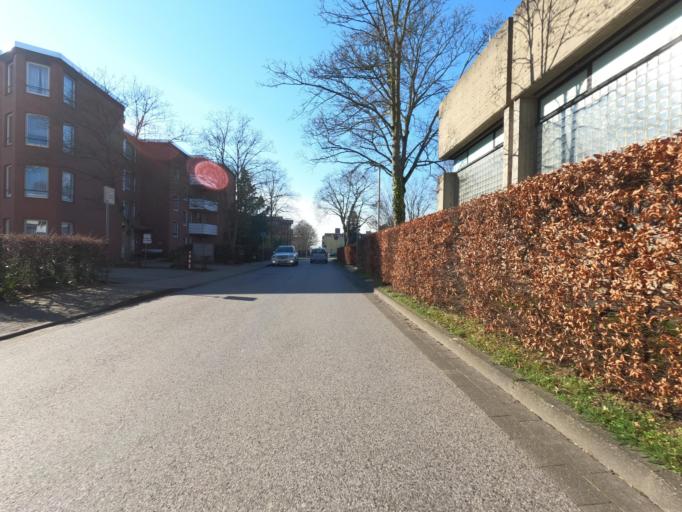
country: DE
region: North Rhine-Westphalia
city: Huckelhoven
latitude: 51.0539
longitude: 6.2259
